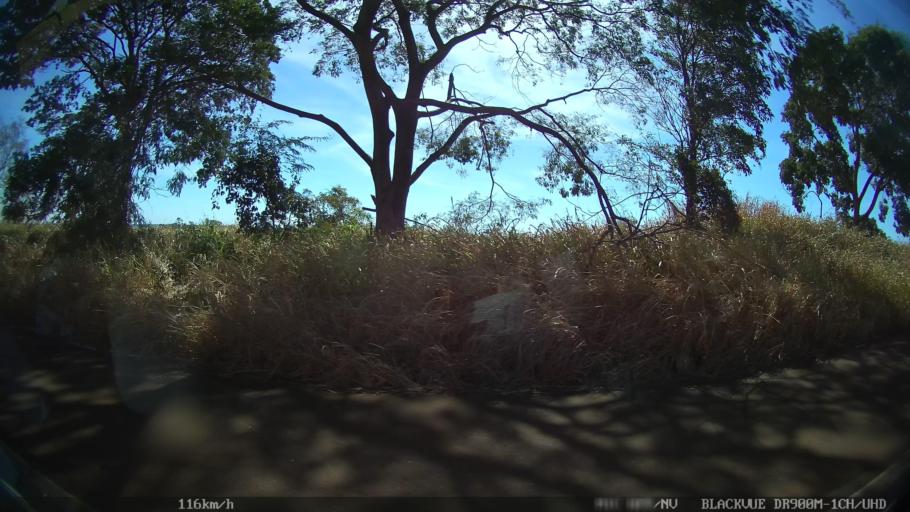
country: BR
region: Sao Paulo
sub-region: Franca
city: Franca
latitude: -20.5613
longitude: -47.6136
